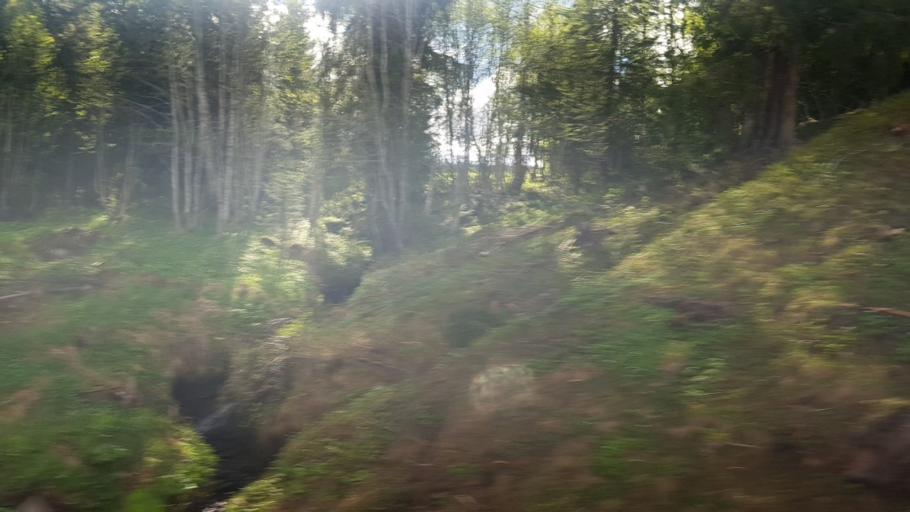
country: NO
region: Sor-Trondelag
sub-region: Rennebu
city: Berkak
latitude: 62.8989
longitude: 10.1103
